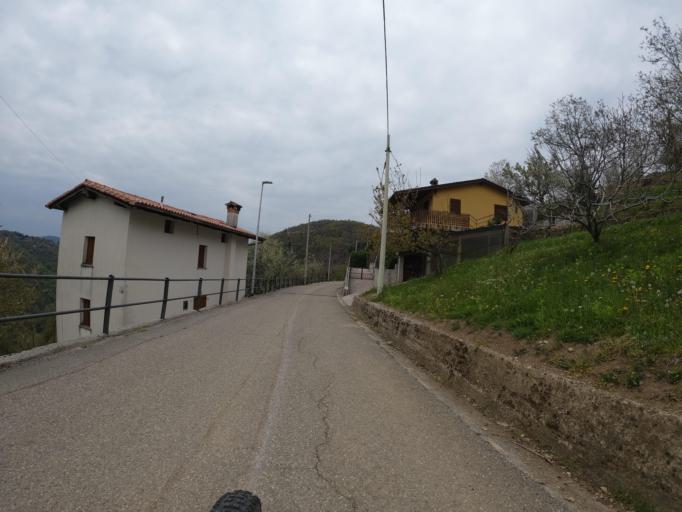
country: IT
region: Friuli Venezia Giulia
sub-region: Provincia di Udine
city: Clodig
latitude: 46.1422
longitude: 13.6051
